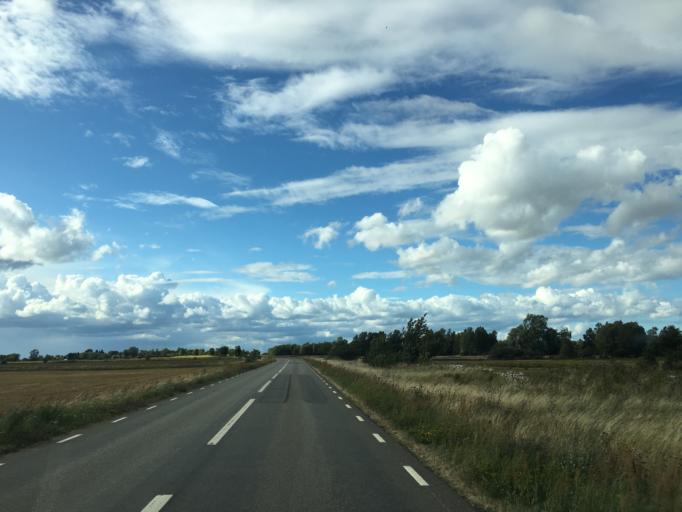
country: SE
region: Kalmar
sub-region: Morbylanga Kommun
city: Moerbylanga
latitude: 56.4345
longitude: 16.4352
